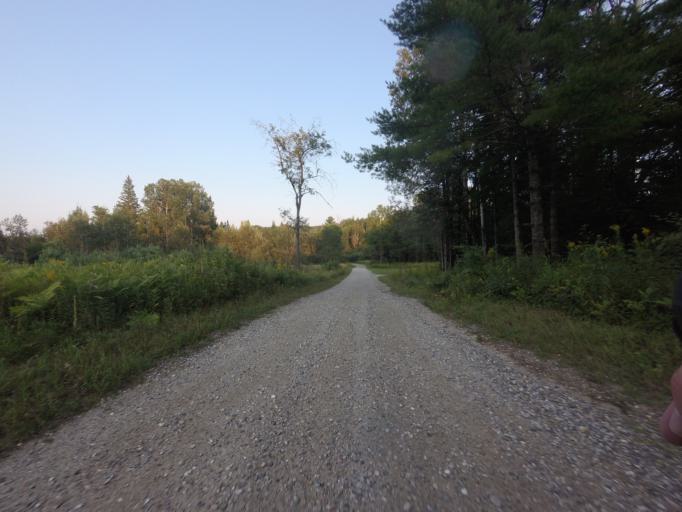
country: CA
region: Ontario
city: Renfrew
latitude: 45.0742
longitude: -76.7429
